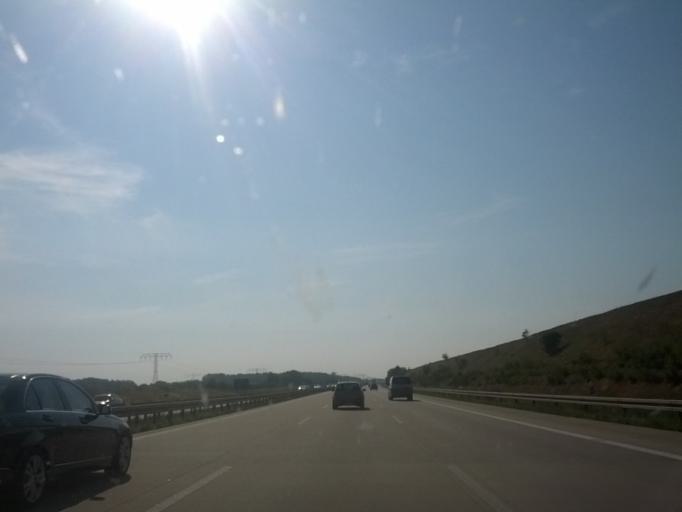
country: DE
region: Brandenburg
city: Neuenhagen
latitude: 52.5321
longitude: 13.7063
